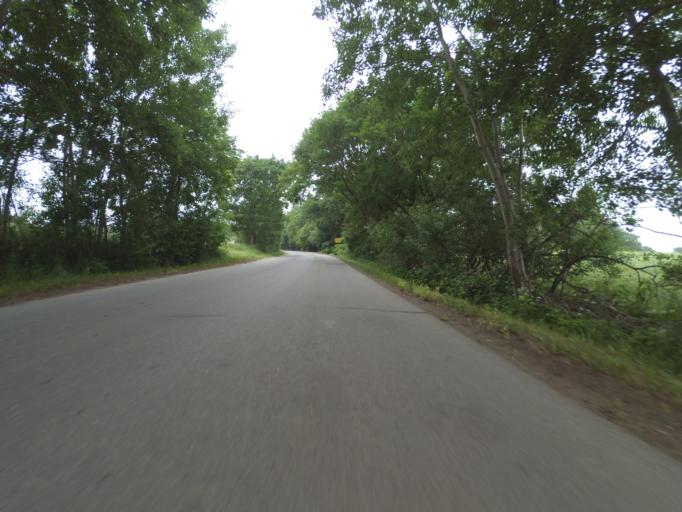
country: DE
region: Mecklenburg-Vorpommern
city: Lubz
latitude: 53.4870
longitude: 11.9793
